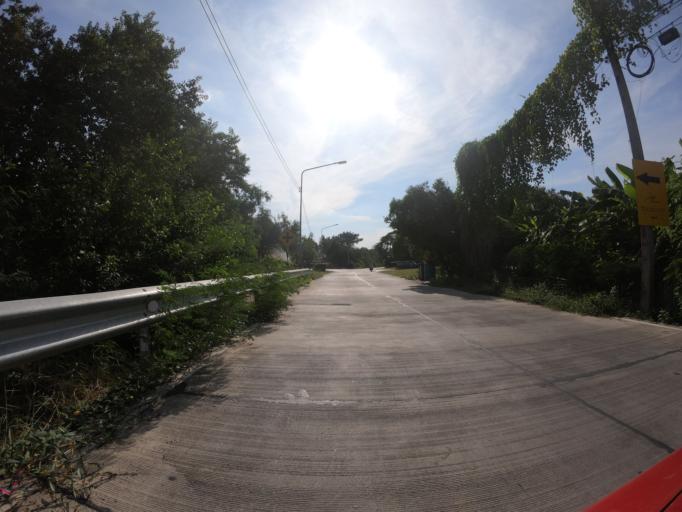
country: TH
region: Pathum Thani
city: Thanyaburi
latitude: 14.0211
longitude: 100.7405
